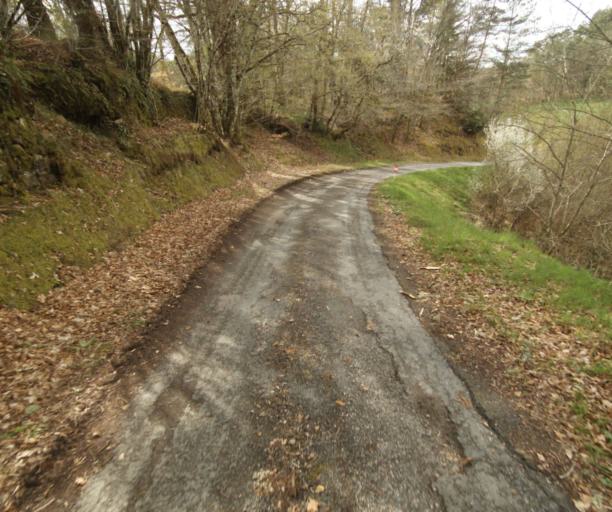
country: FR
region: Limousin
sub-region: Departement de la Correze
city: Argentat
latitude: 45.1864
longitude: 1.9489
